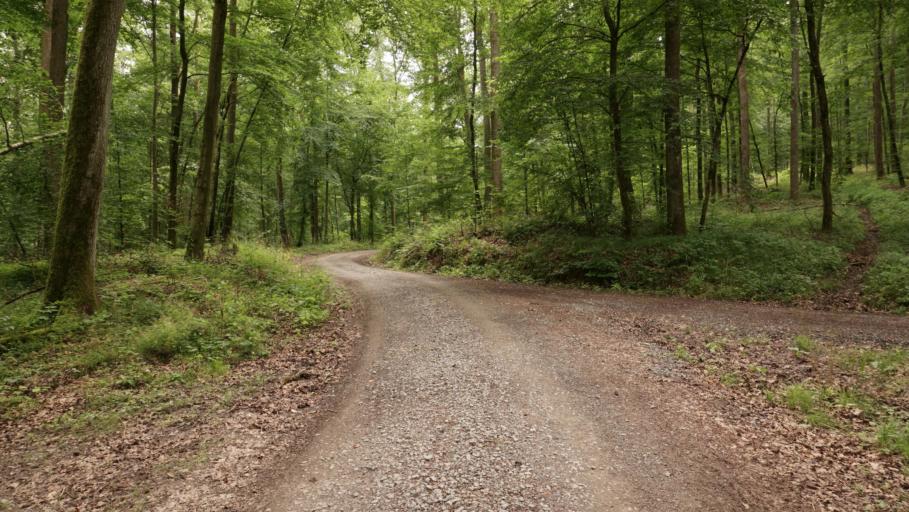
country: DE
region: Baden-Wuerttemberg
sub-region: Karlsruhe Region
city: Billigheim
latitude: 49.3209
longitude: 9.2068
